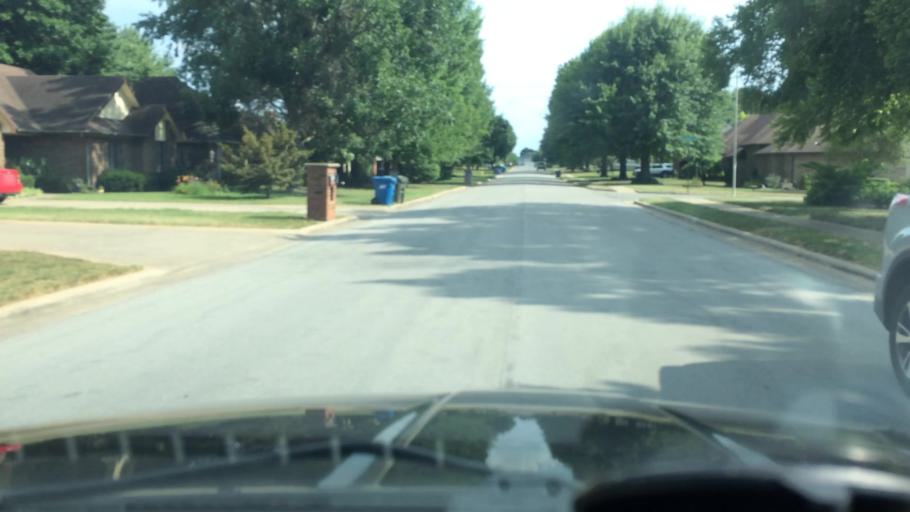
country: US
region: Missouri
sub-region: Greene County
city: Springfield
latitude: 37.2681
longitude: -93.2667
